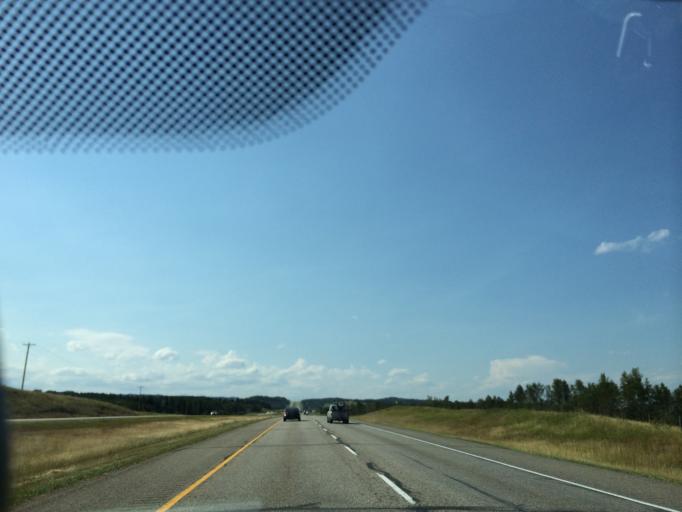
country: CA
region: Alberta
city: Cochrane
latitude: 51.1217
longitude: -114.6702
